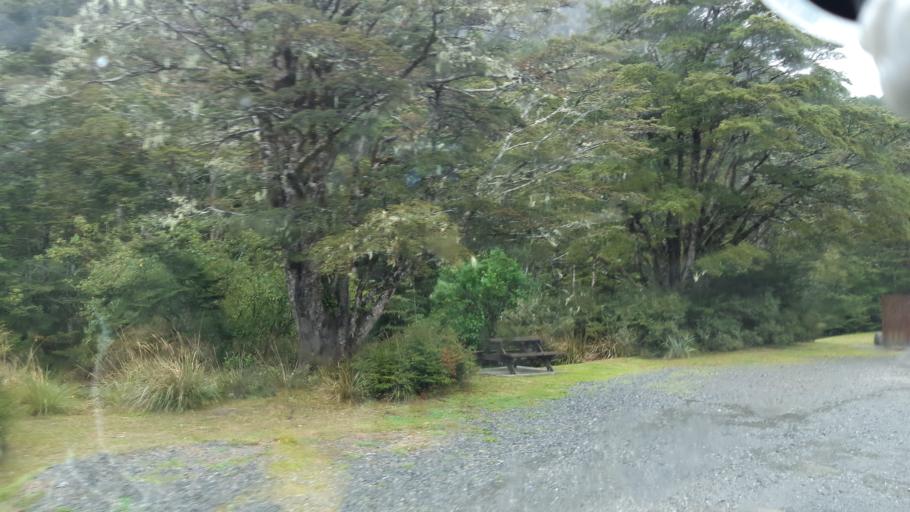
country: NZ
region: Canterbury
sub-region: Hurunui District
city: Amberley
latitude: -42.4048
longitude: 172.3975
